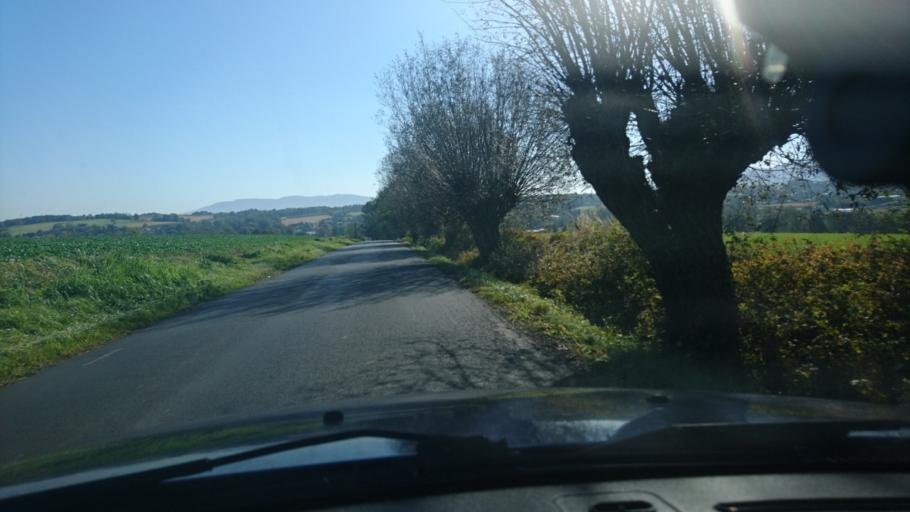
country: PL
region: Silesian Voivodeship
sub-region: Powiat bielski
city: Bronow
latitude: 49.8546
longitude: 18.9288
